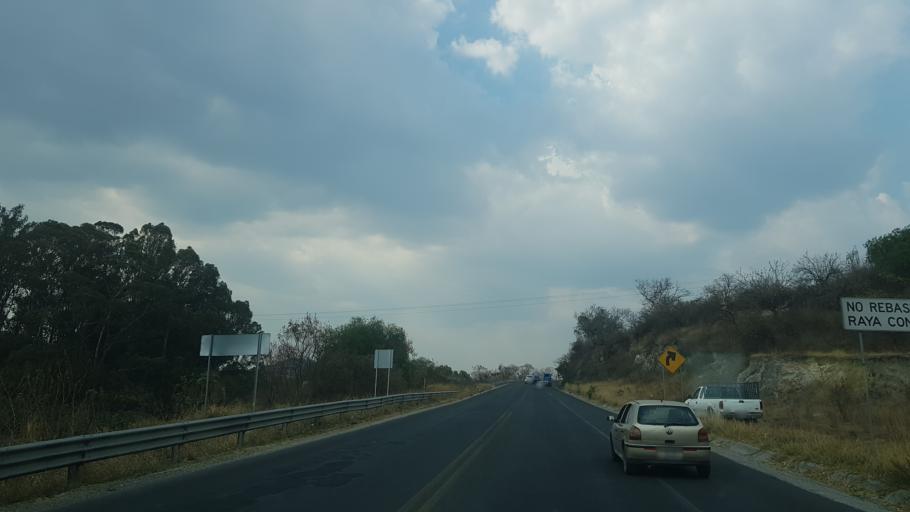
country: MX
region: Puebla
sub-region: Santa Isabel Cholula
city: Santa Ana Acozautla
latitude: 18.9503
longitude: -98.3891
